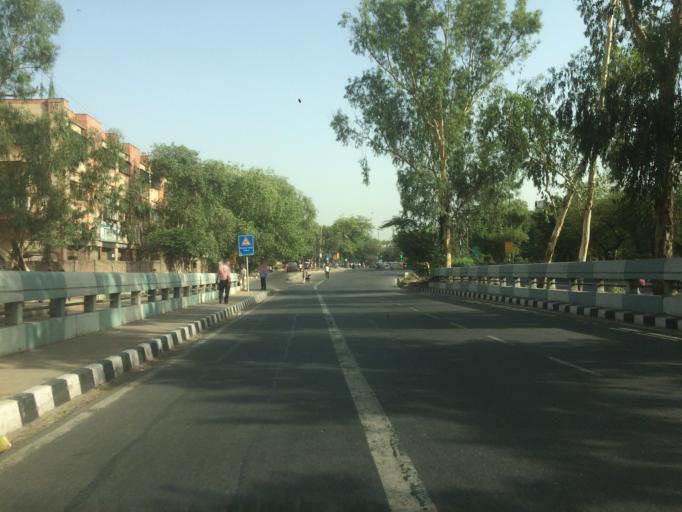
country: IN
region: Uttar Pradesh
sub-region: Gautam Buddha Nagar
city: Noida
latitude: 28.5599
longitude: 77.2680
